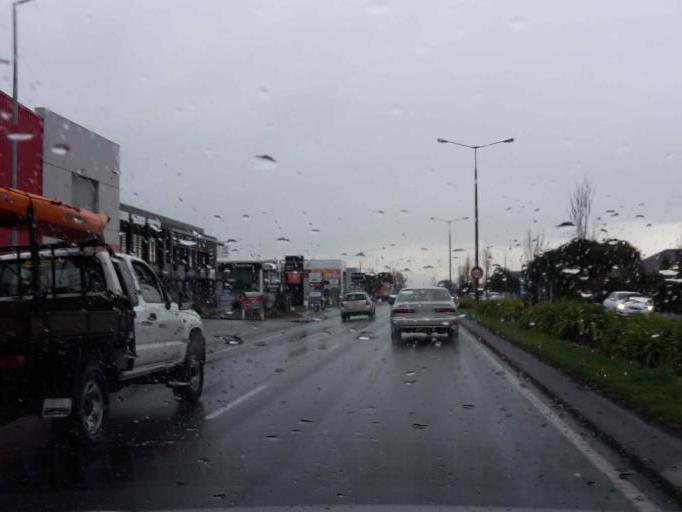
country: NZ
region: Canterbury
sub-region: Christchurch City
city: Christchurch
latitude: -43.5385
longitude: 172.5841
